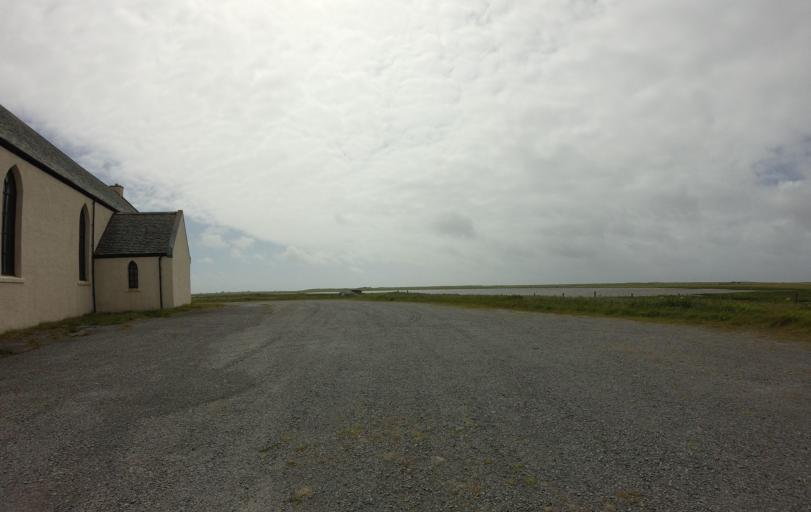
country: GB
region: Scotland
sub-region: Eilean Siar
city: Isle of South Uist
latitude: 57.2411
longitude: -7.4181
